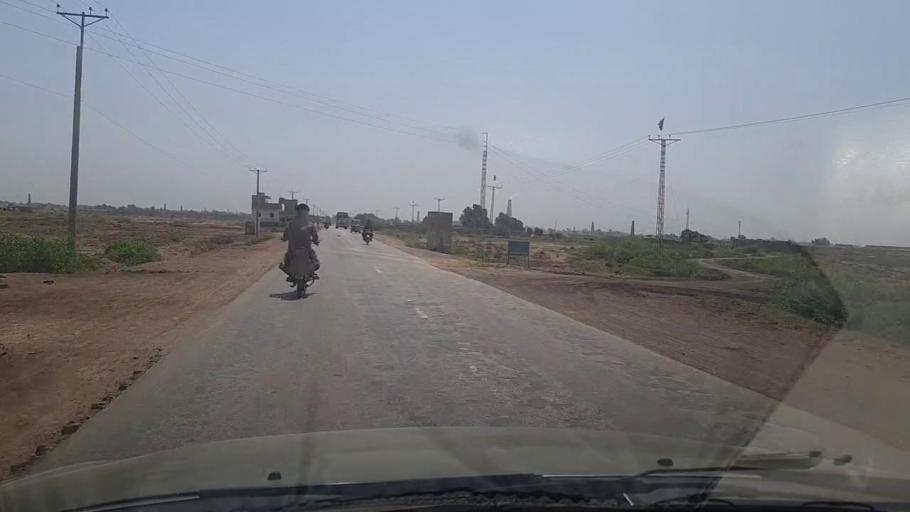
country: PK
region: Sindh
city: Hyderabad
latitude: 25.3840
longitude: 68.4387
